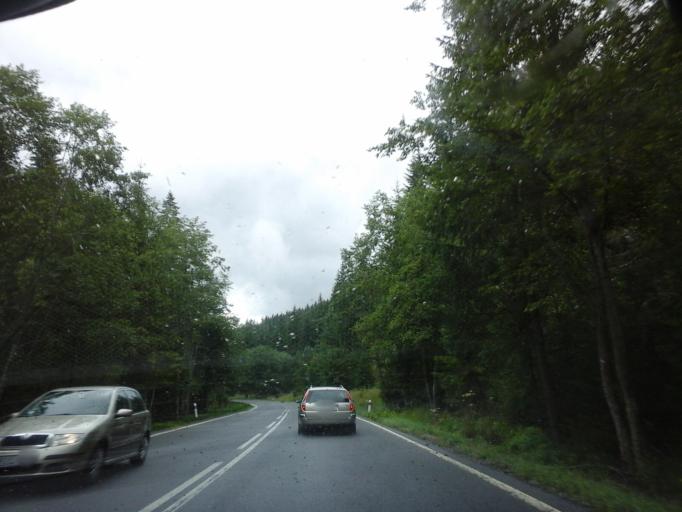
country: SK
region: Kosicky
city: Dobsina
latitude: 48.8848
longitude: 20.2473
